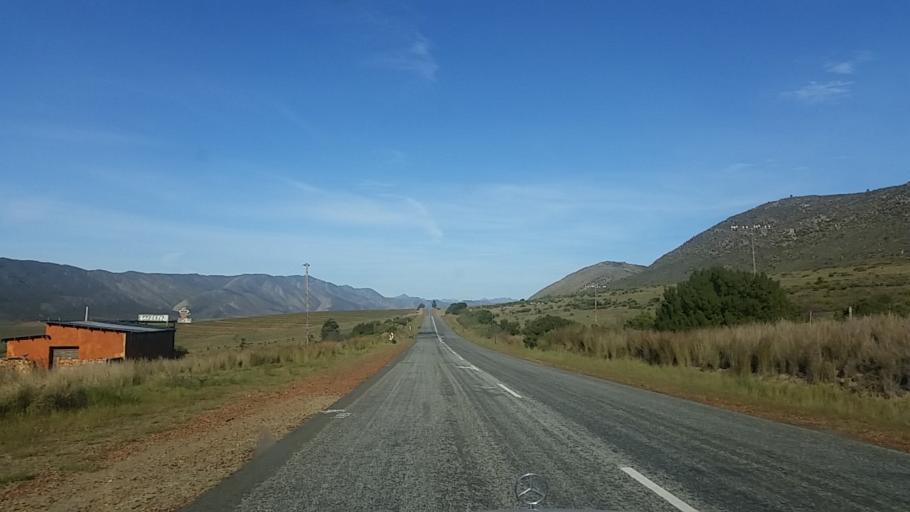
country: ZA
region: Western Cape
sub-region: Eden District Municipality
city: Knysna
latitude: -33.7727
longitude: 22.9295
